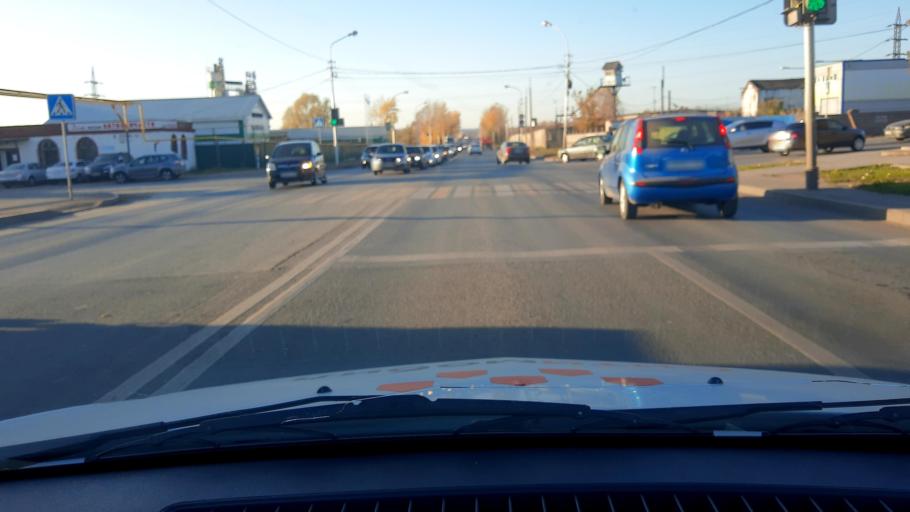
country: RU
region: Bashkortostan
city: Iglino
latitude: 54.7821
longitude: 56.2245
